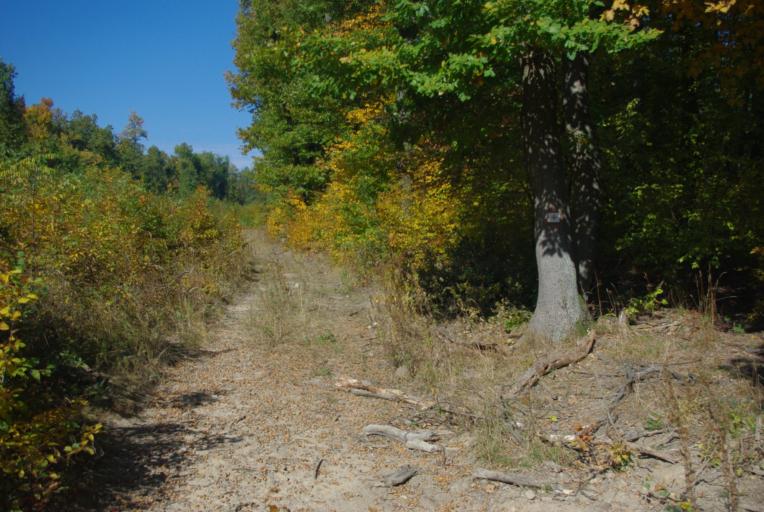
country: HU
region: Pest
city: Budakeszi
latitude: 47.5440
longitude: 18.8926
